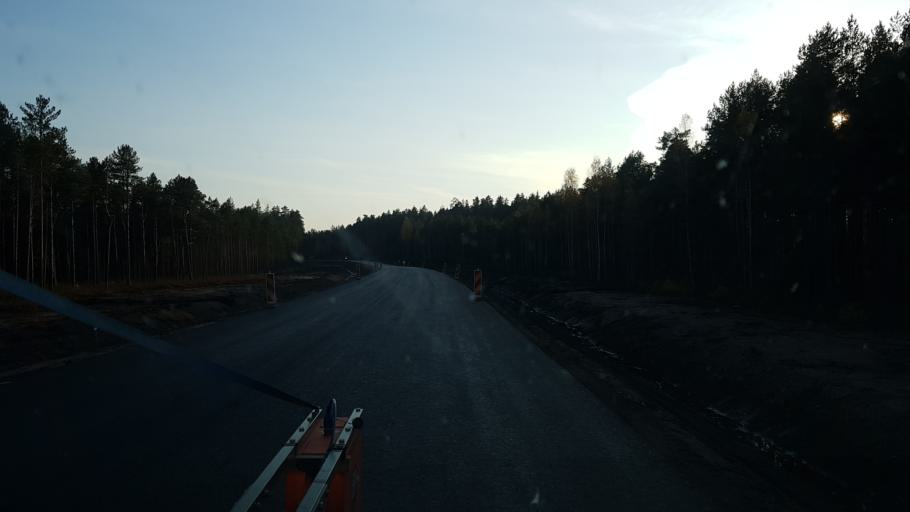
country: EE
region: Polvamaa
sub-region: Polva linn
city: Polva
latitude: 57.9323
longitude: 27.1854
